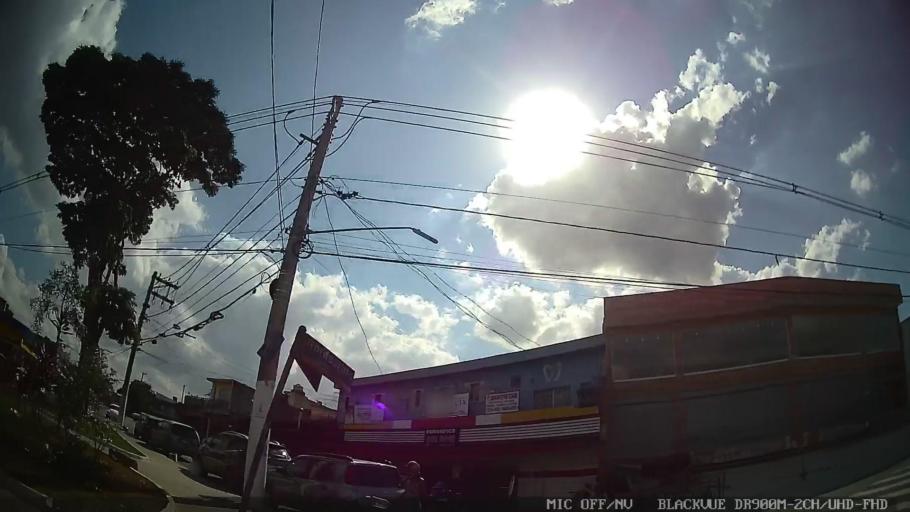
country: BR
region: Sao Paulo
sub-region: Ferraz De Vasconcelos
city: Ferraz de Vasconcelos
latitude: -23.5271
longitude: -46.4180
